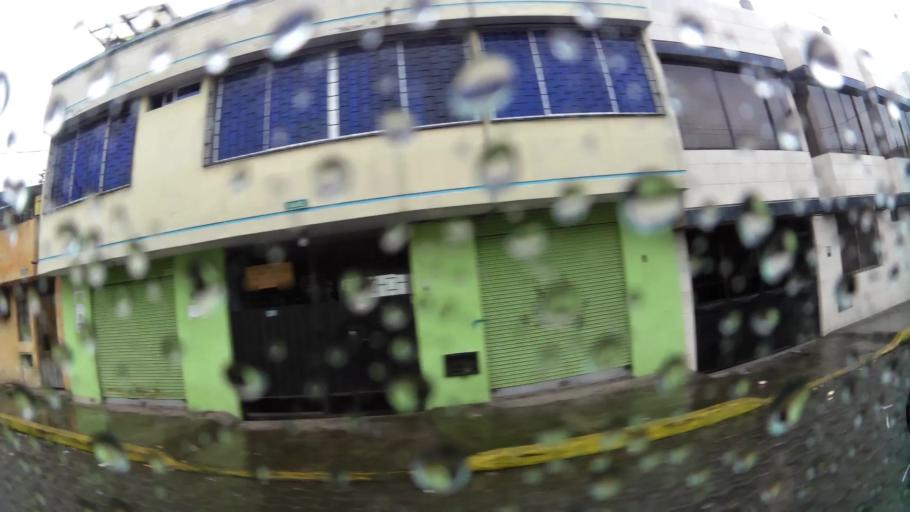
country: EC
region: Pichincha
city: Quito
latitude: -0.3223
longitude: -78.5543
